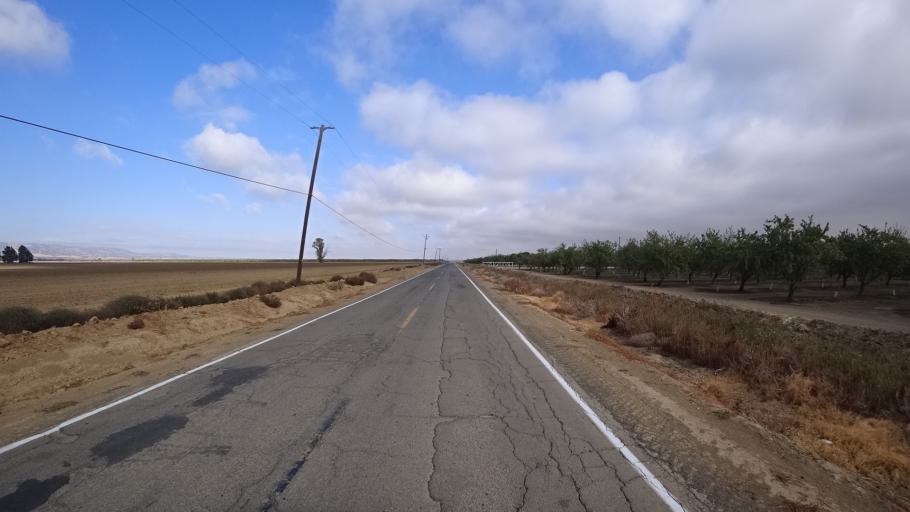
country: US
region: California
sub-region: Yolo County
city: Esparto
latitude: 38.7451
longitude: -122.0074
